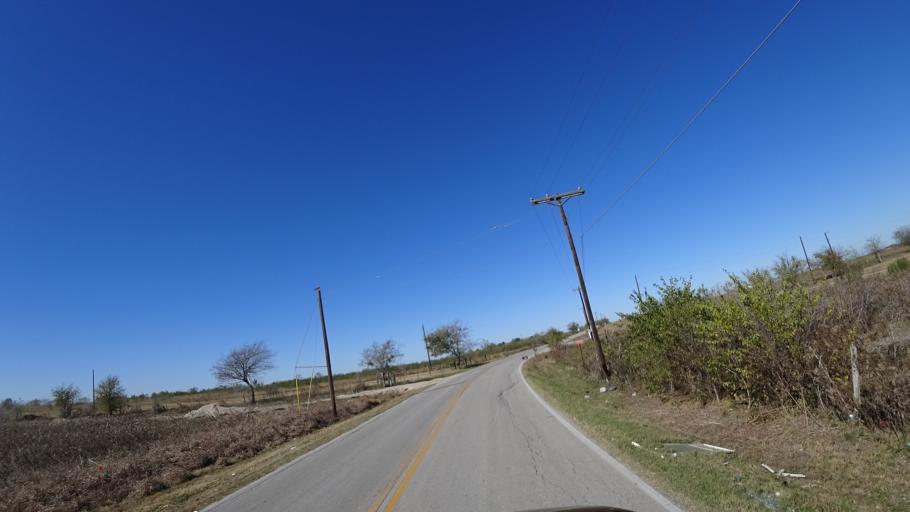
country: US
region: Texas
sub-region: Travis County
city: Garfield
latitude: 30.1239
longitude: -97.5989
